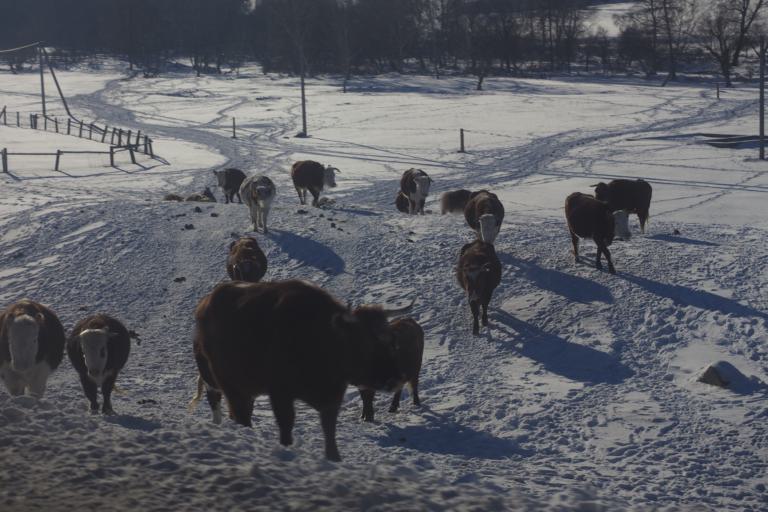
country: RU
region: Altay
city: Onguday
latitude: 50.6624
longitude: 86.2873
